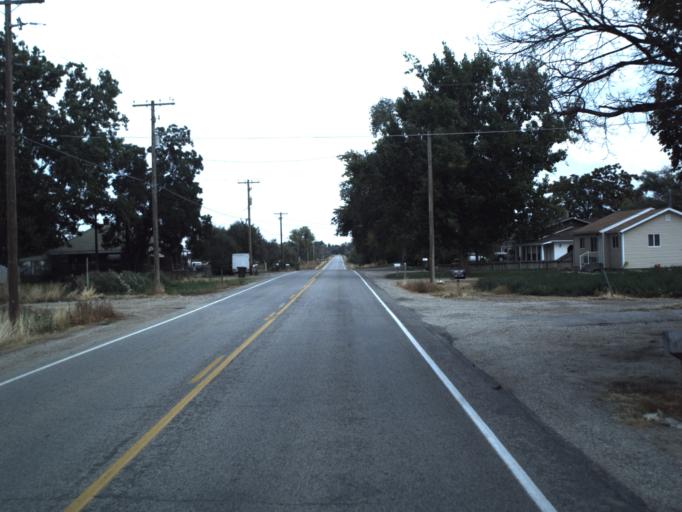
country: US
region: Utah
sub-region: Weber County
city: Plain City
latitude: 41.2658
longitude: -112.0924
